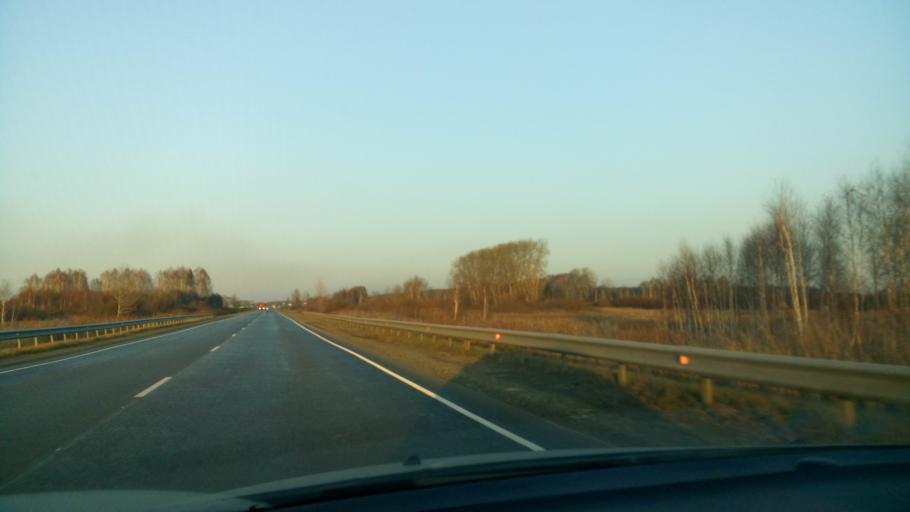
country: RU
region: Sverdlovsk
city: Obukhovskoye
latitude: 56.8314
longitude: 62.5667
